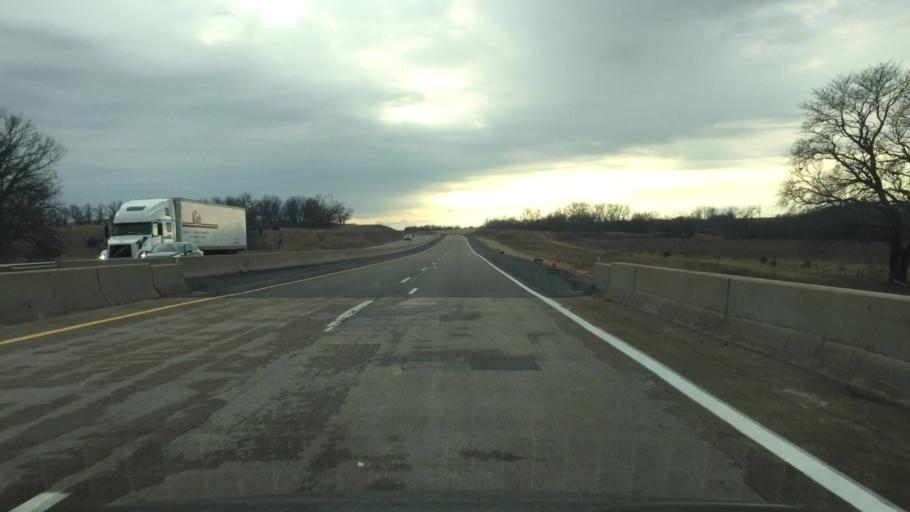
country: US
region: Kansas
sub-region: Lyon County
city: Emporia
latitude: 38.6045
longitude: -96.0647
